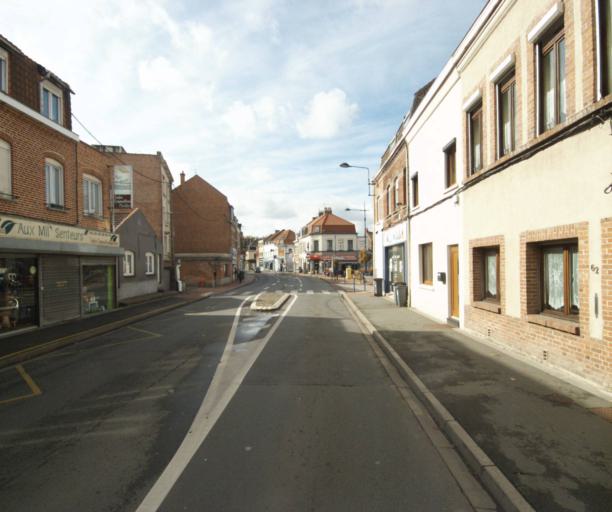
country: FR
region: Nord-Pas-de-Calais
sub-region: Departement du Nord
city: Houplines
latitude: 50.6889
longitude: 2.9027
